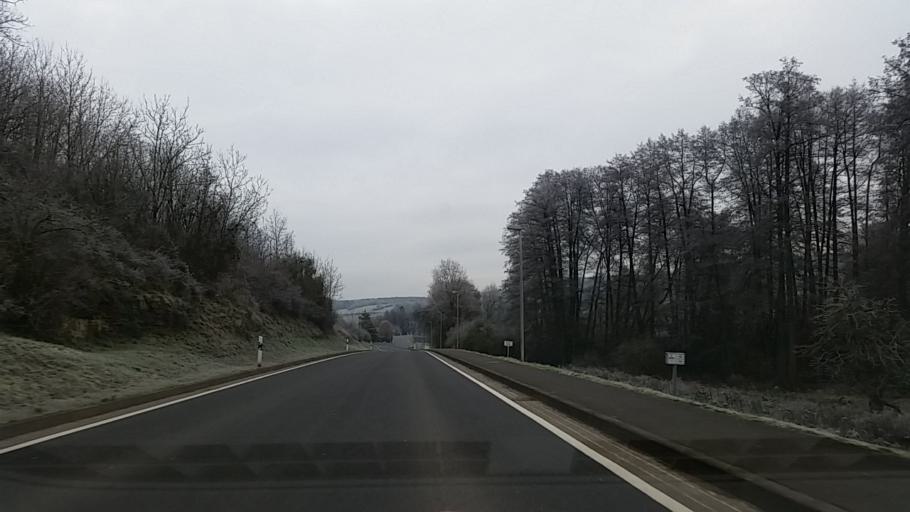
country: DE
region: Bavaria
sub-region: Regierungsbezirk Unterfranken
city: Eussenheim
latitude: 50.0151
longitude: 9.8584
